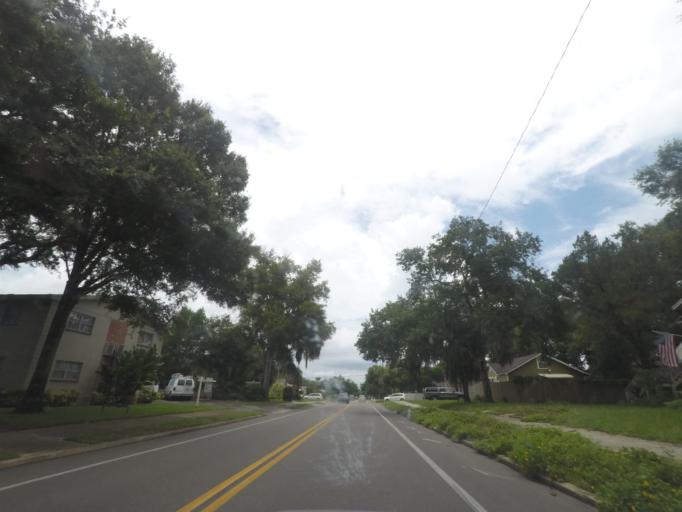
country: US
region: Florida
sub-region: Pinellas County
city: Lealman
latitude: 27.7994
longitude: -82.6414
